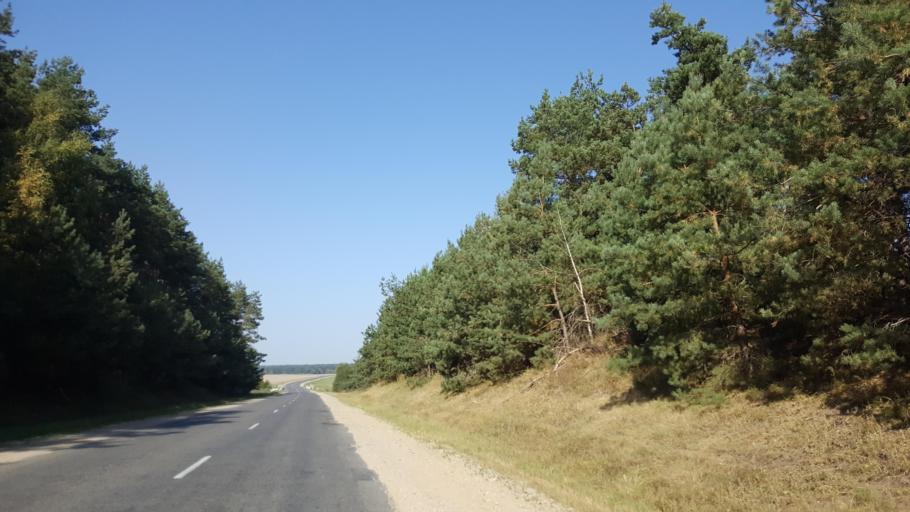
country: BY
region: Brest
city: Kamyanyets
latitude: 52.4084
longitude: 23.7355
